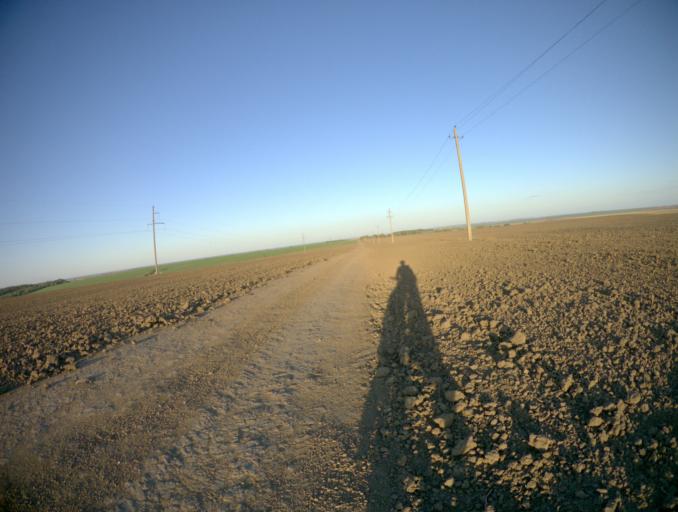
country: RU
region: Ivanovo
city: Gavrilov Posad
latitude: 56.4191
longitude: 40.1839
